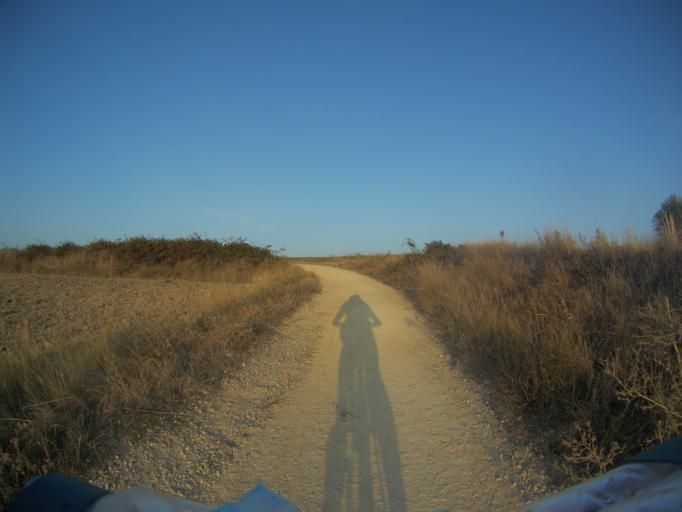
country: ES
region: Navarre
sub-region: Provincia de Navarra
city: Bargota
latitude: 42.5412
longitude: -2.3055
